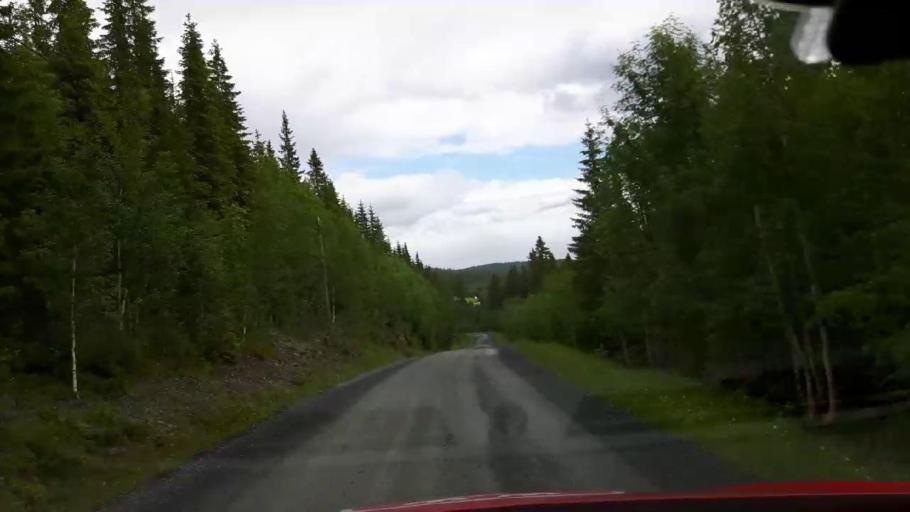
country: NO
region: Nord-Trondelag
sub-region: Lierne
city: Sandvika
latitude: 64.1596
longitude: 14.0409
